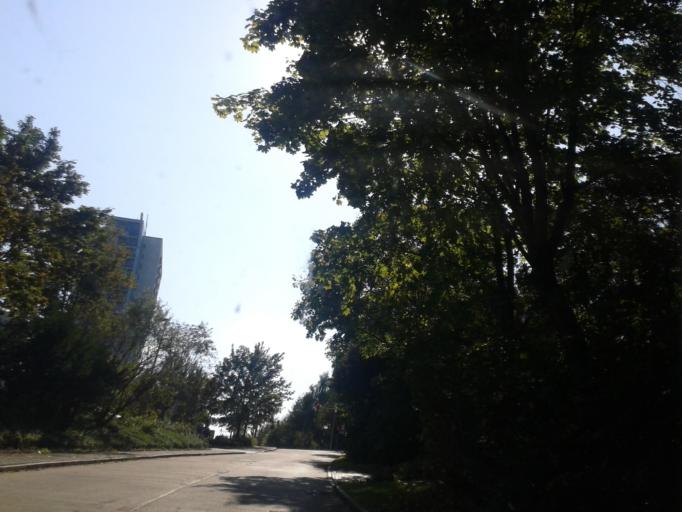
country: DE
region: Saxony
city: Dresden
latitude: 51.0247
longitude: 13.7420
